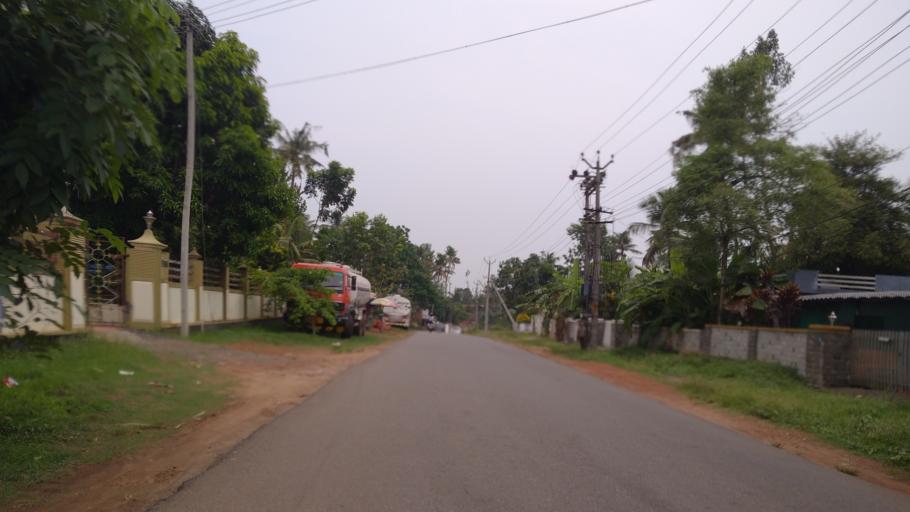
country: IN
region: Kerala
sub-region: Ernakulam
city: Angamali
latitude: 10.1775
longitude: 76.3983
